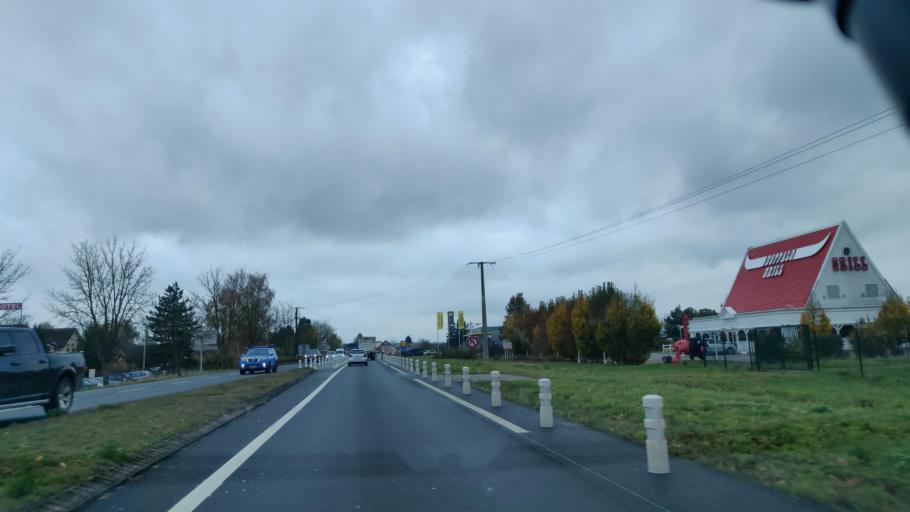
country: FR
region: Lorraine
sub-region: Departement de Meurthe-et-Moselle
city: Chanteheux
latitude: 48.5701
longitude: 6.5337
